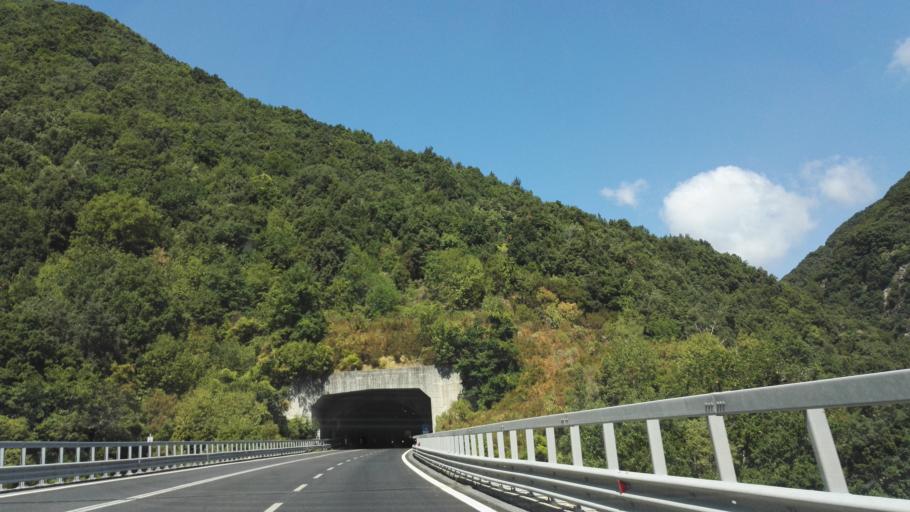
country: IT
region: Calabria
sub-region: Provincia di Reggio Calabria
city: Canolo
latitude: 38.3631
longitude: 16.1893
